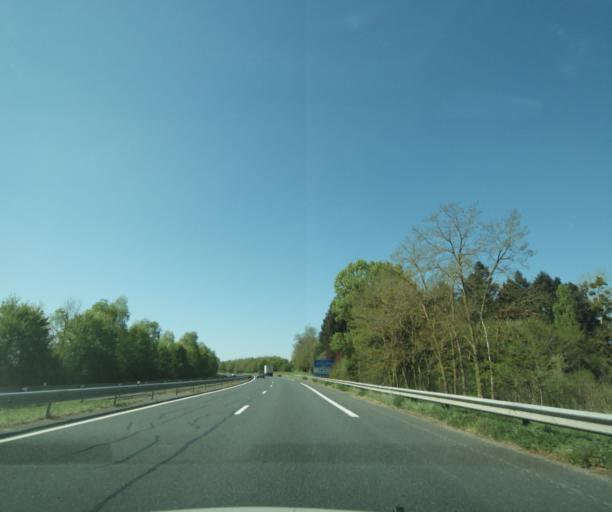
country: FR
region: Centre
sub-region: Departement du Cher
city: Gracay
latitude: 47.0970
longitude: 1.8628
